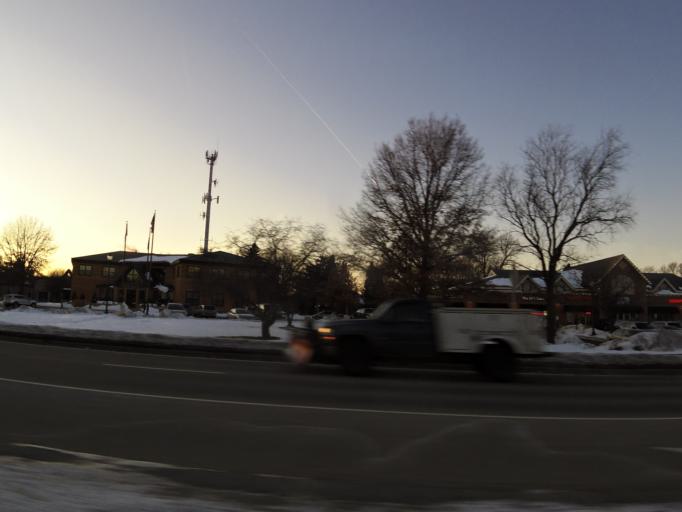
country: US
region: Minnesota
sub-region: Ramsey County
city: White Bear Lake
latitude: 45.0838
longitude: -93.0111
